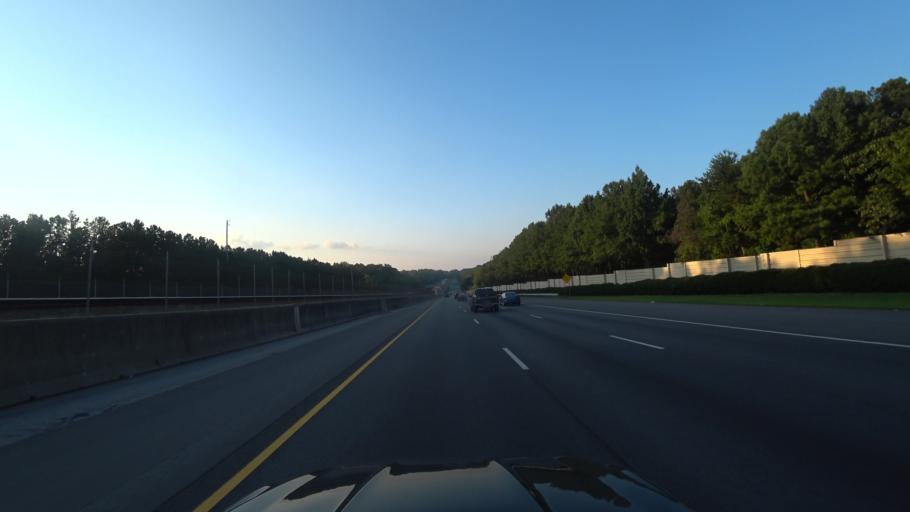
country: US
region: Georgia
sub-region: DeKalb County
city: North Atlanta
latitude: 33.8780
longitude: -84.3646
